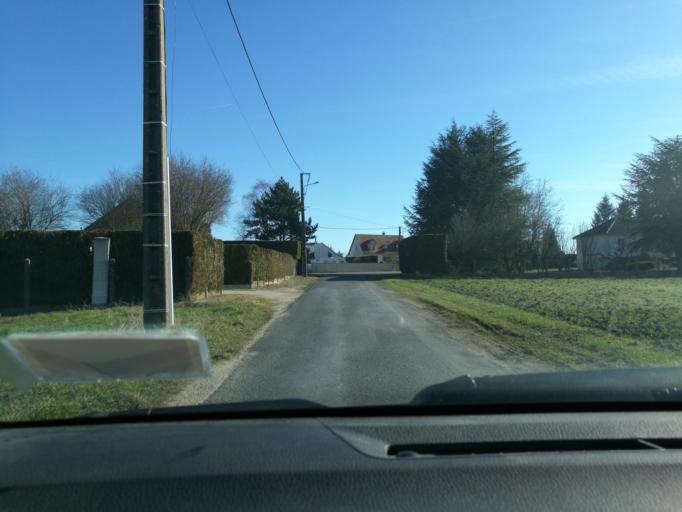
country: FR
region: Centre
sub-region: Departement du Loiret
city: Chaingy
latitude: 47.8880
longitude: 1.7662
